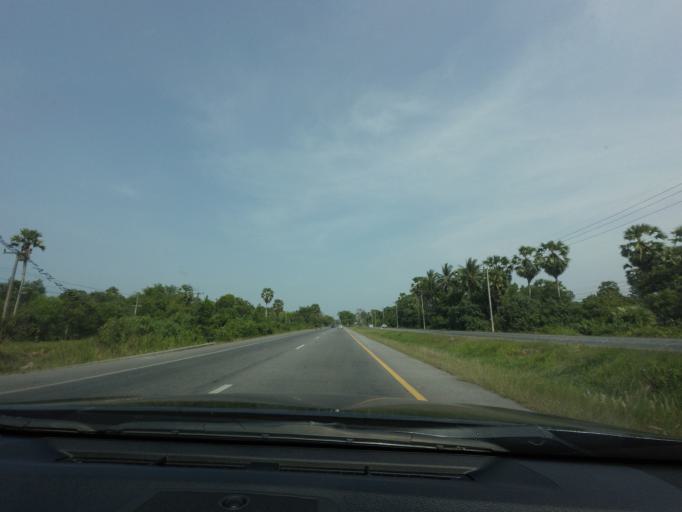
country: TH
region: Pattani
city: Yaring
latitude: 6.8233
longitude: 101.4003
